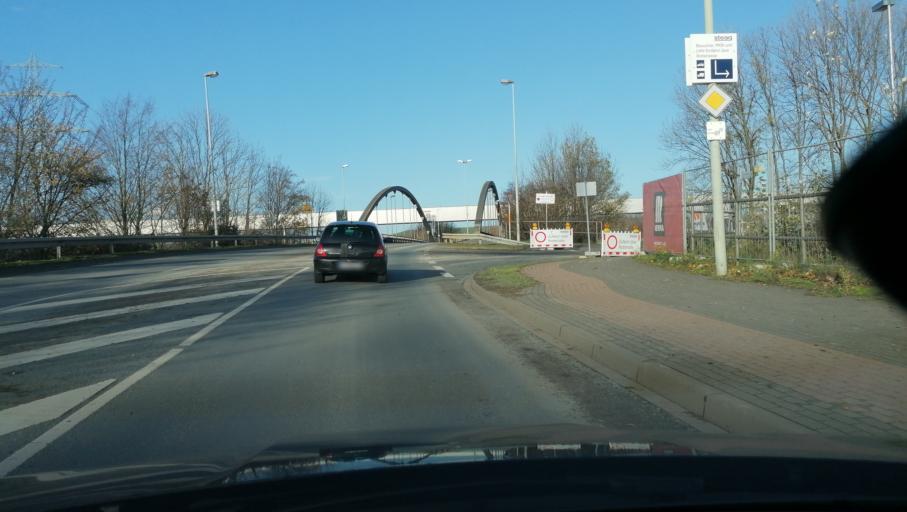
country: DE
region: North Rhine-Westphalia
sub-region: Regierungsbezirk Arnsberg
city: Herne
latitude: 51.5491
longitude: 7.1794
